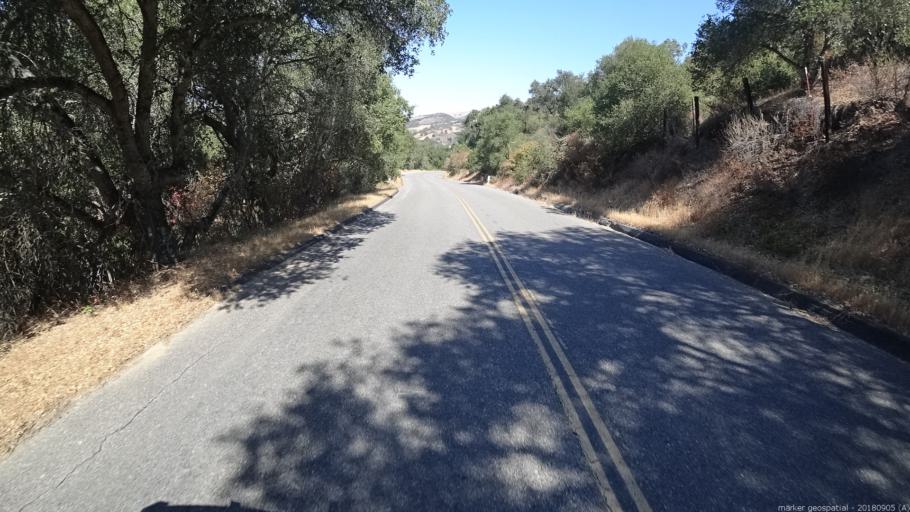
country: US
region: California
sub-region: Monterey County
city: Gonzales
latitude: 36.4086
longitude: -121.5932
